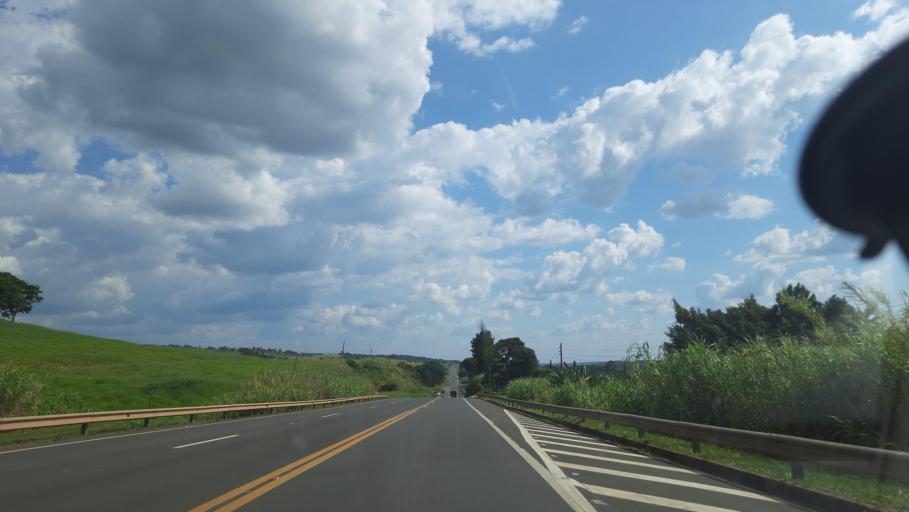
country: BR
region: Sao Paulo
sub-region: Sao Jose Do Rio Pardo
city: Sao Jose do Rio Pardo
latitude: -21.6625
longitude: -46.9183
